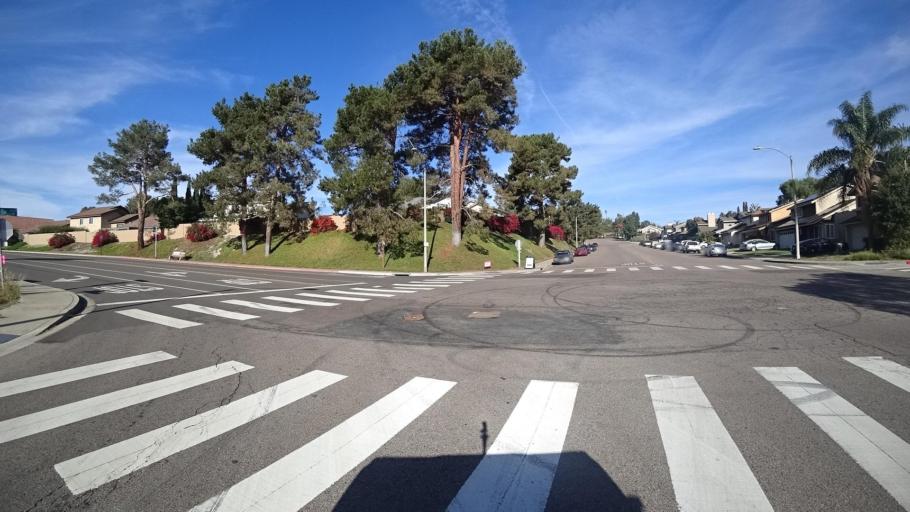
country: US
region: California
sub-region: San Diego County
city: Rancho San Diego
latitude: 32.7334
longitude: -116.9630
